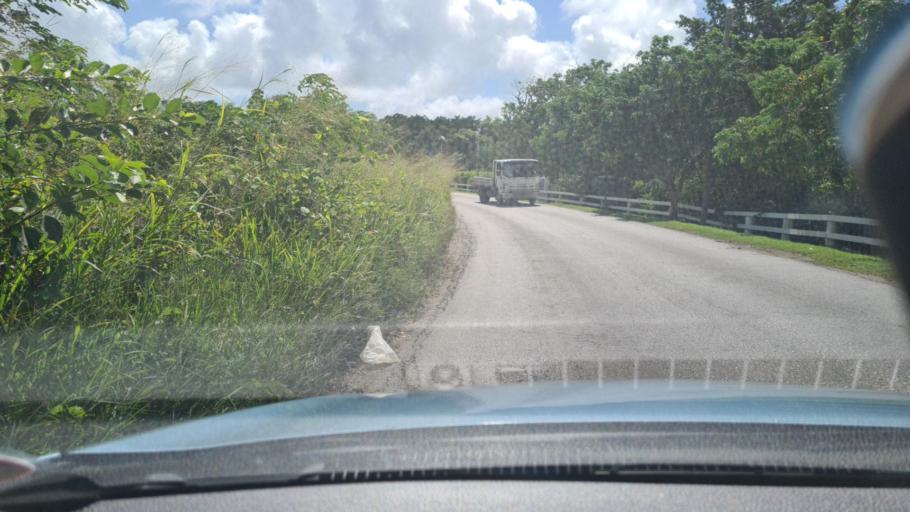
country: BB
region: Christ Church
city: Oistins
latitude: 13.0900
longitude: -59.5205
